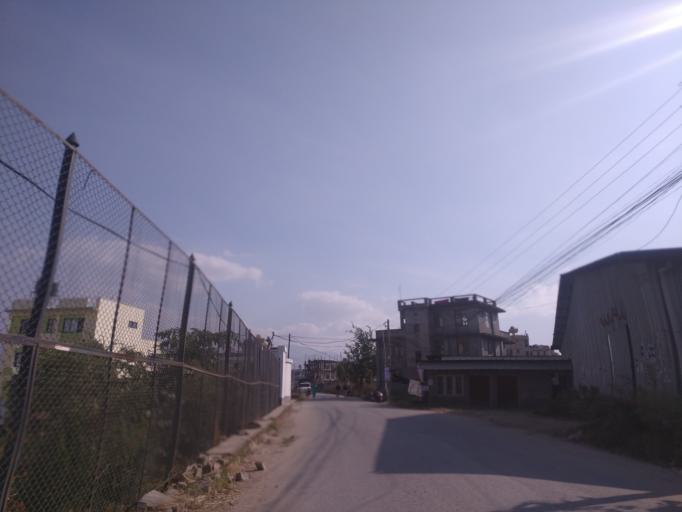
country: NP
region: Central Region
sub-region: Bagmati Zone
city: Patan
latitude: 27.6771
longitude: 85.3322
